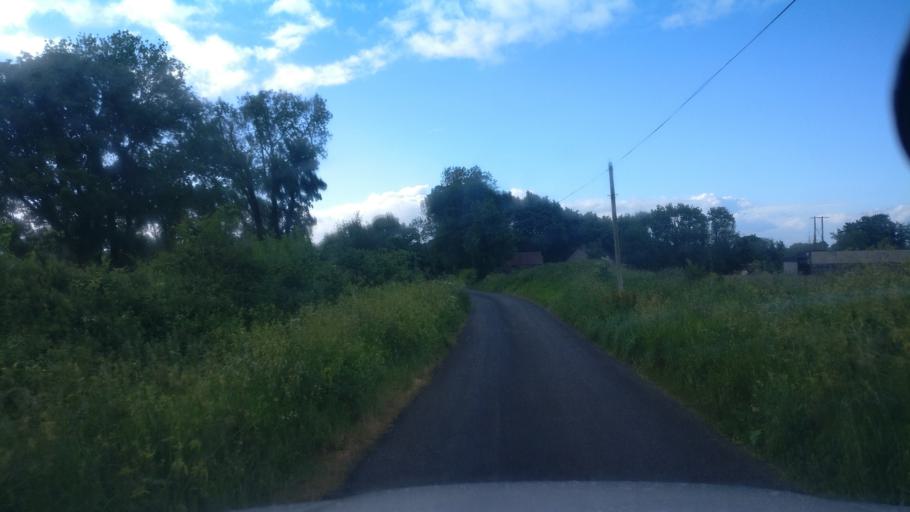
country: IE
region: Connaught
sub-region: County Galway
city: Ballinasloe
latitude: 53.2428
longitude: -8.2287
